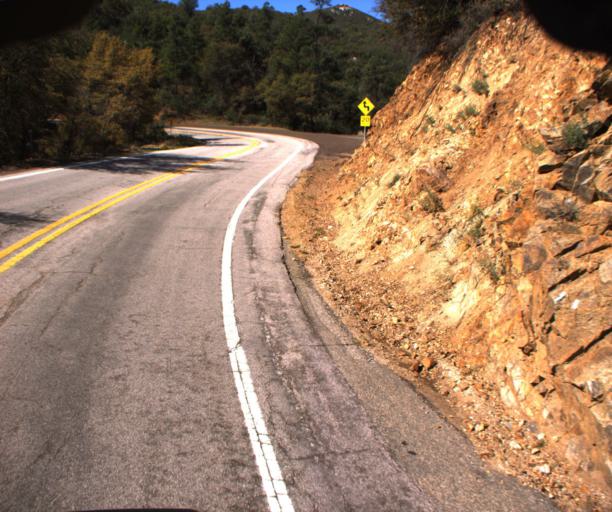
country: US
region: Arizona
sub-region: Yavapai County
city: Prescott
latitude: 34.4397
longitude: -112.5472
